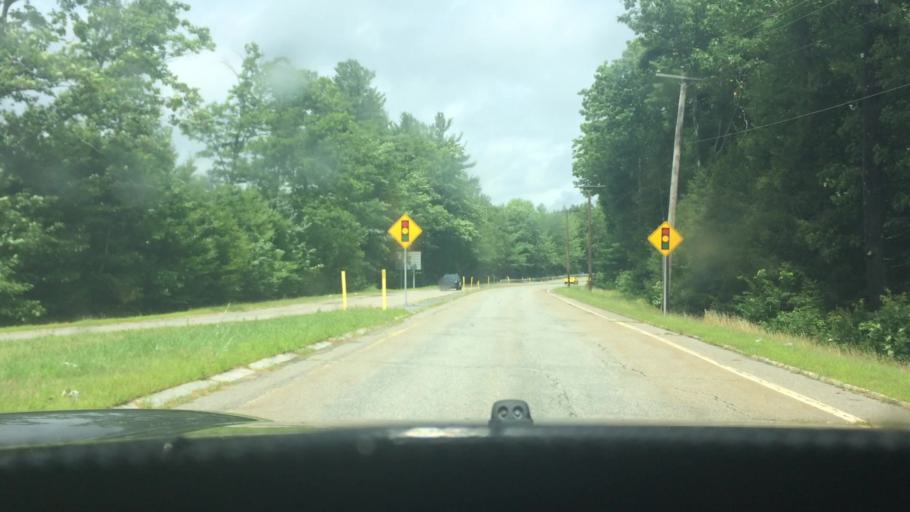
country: US
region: Massachusetts
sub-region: Worcester County
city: Athol
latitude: 42.5777
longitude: -72.1798
